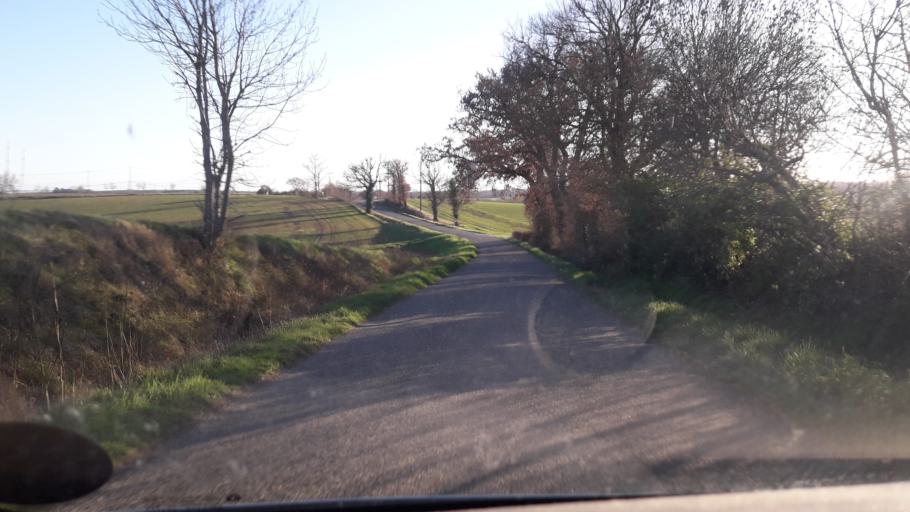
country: FR
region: Midi-Pyrenees
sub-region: Departement du Gers
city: Gimont
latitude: 43.6279
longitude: 0.9756
